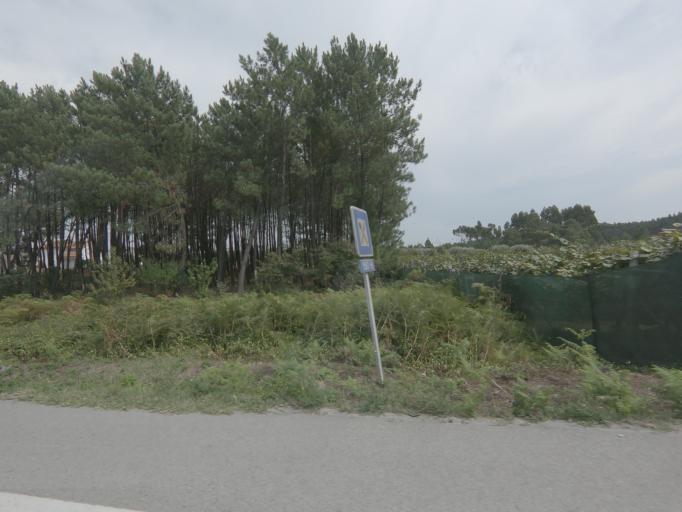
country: PT
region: Leiria
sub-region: Pombal
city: Pombal
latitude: 39.8715
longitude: -8.6908
